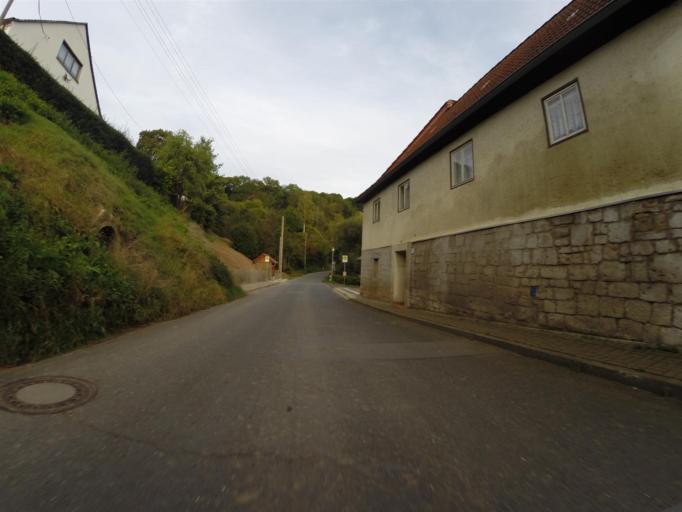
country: DE
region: Thuringia
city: Lehesten
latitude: 50.9911
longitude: 11.5968
